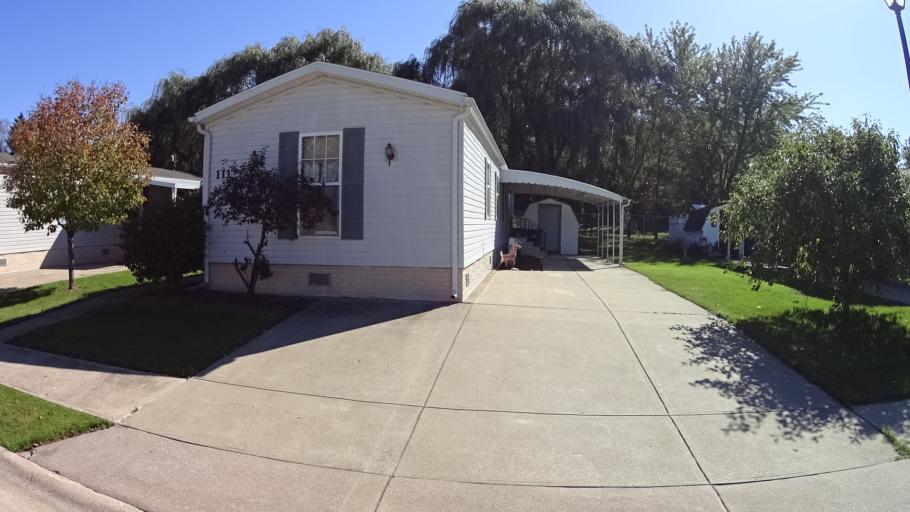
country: US
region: Ohio
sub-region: Lorain County
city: Amherst
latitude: 41.4100
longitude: -82.2003
